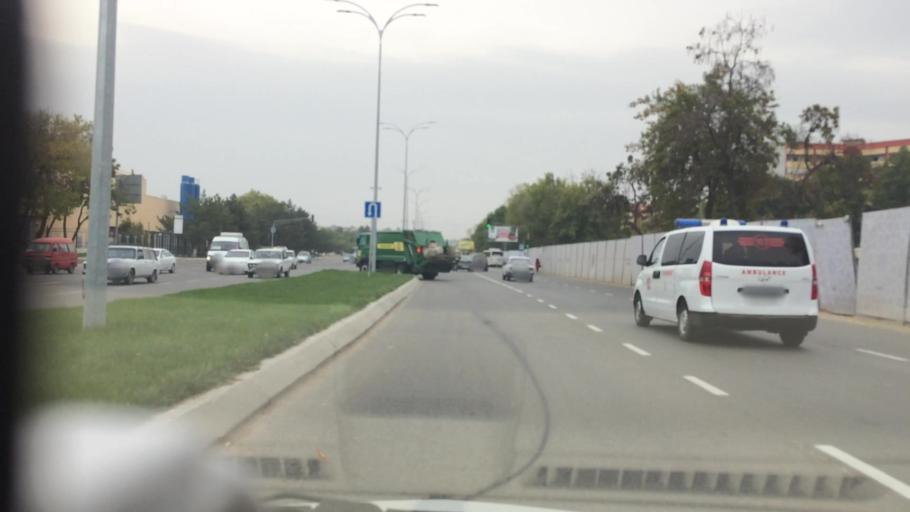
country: UZ
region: Toshkent
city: Salor
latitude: 41.3004
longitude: 69.3460
